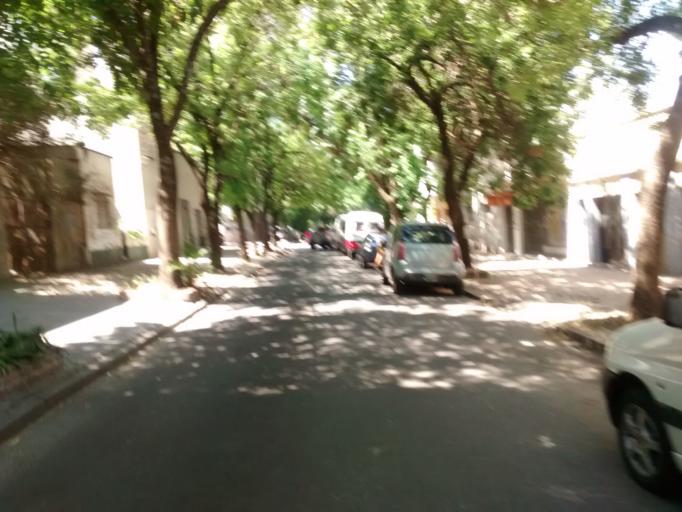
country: AR
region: Buenos Aires
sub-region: Partido de La Plata
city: La Plata
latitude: -34.9260
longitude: -57.9450
